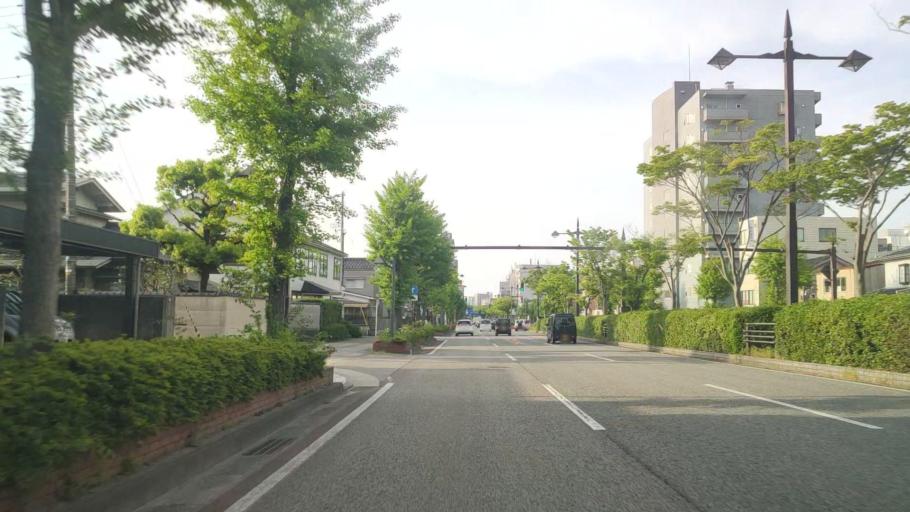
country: JP
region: Toyama
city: Toyama-shi
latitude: 36.6850
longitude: 137.2118
